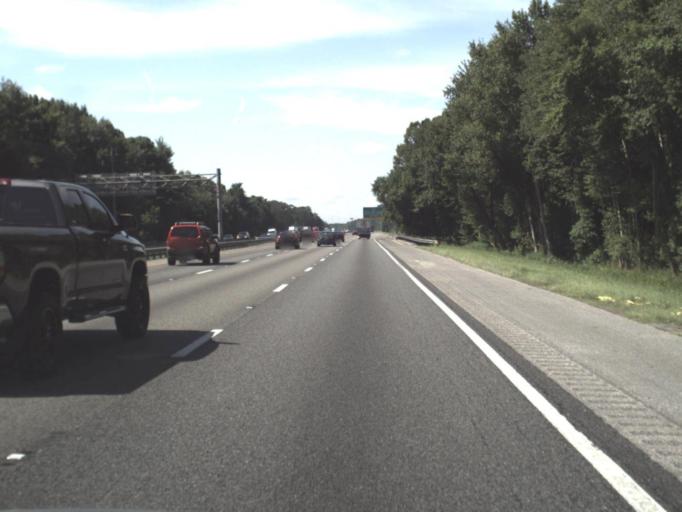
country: US
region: Florida
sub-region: Saint Johns County
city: Palm Valley
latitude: 30.0876
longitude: -81.4979
